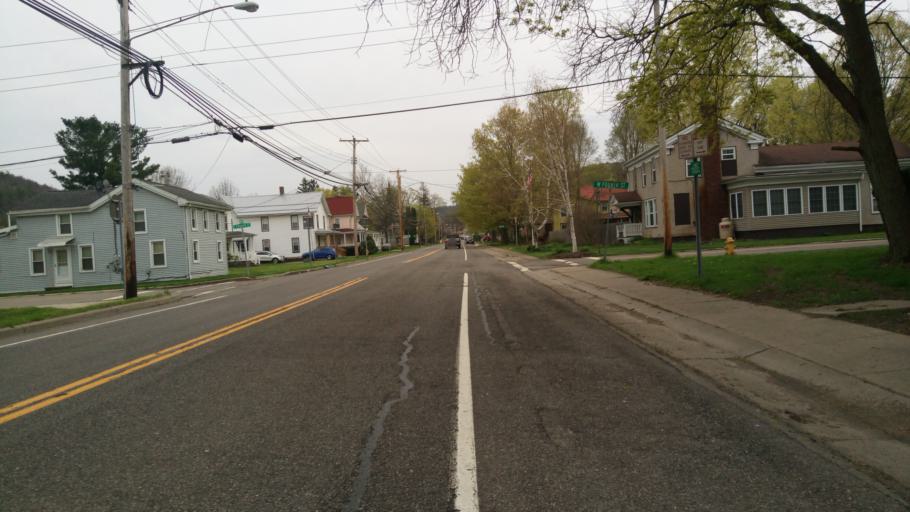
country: US
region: New York
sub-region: Chemung County
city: Southport
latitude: 42.0139
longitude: -76.7280
